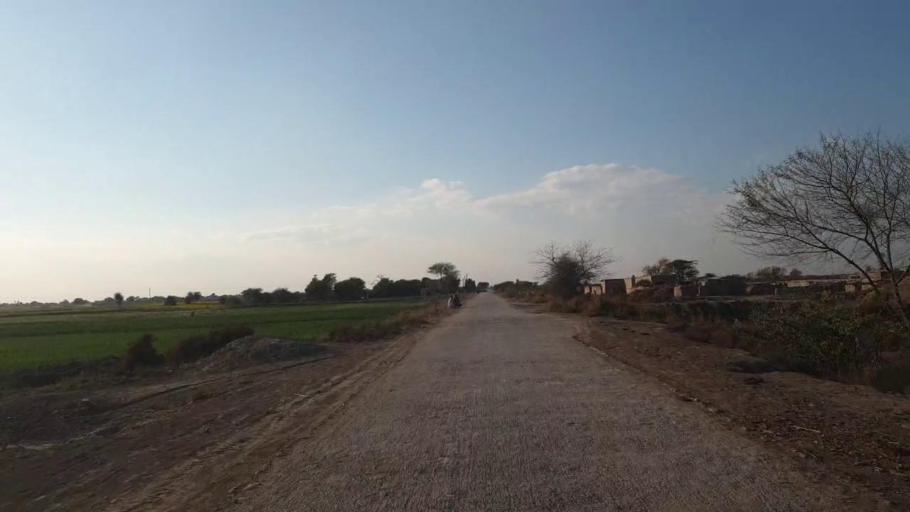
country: PK
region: Sindh
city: Shahpur Chakar
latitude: 26.1434
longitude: 68.5422
